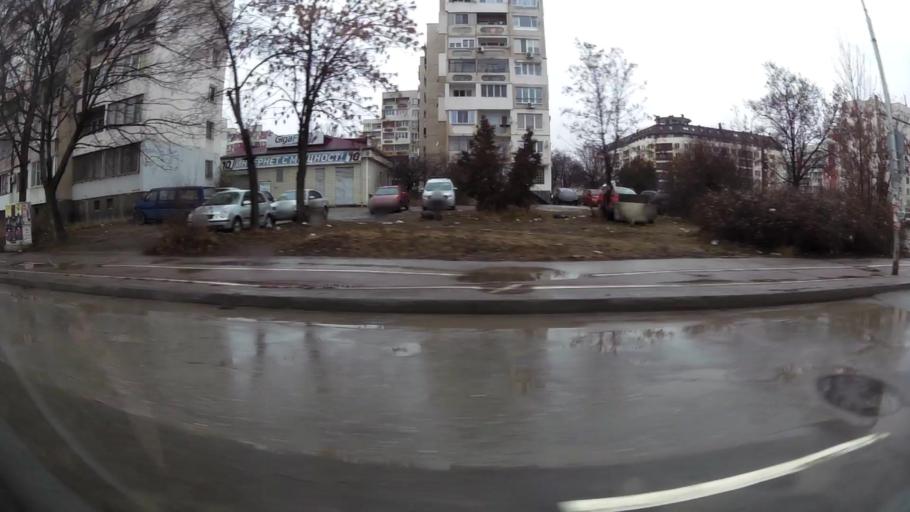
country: BG
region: Sofia-Capital
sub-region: Stolichna Obshtina
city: Sofia
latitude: 42.6331
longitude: 23.3802
